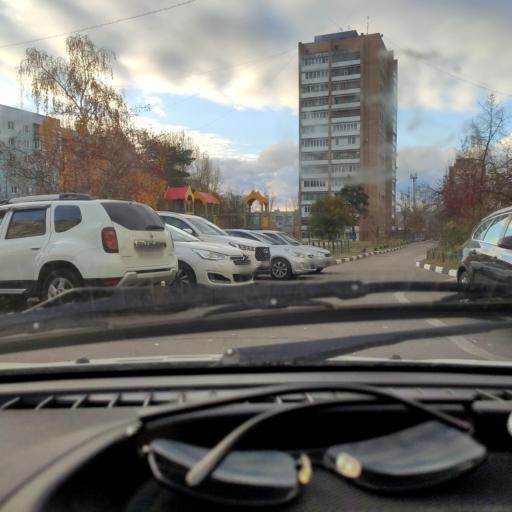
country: RU
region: Samara
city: Zhigulevsk
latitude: 53.4815
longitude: 49.4552
